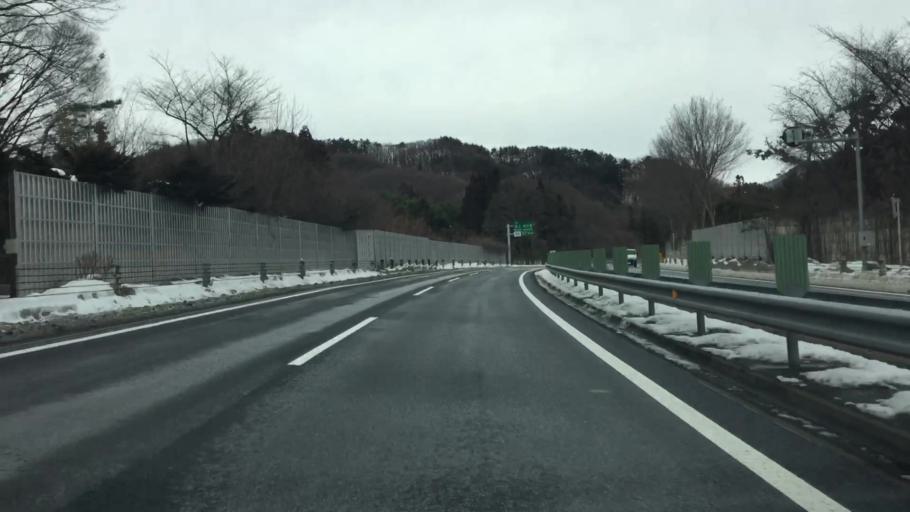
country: JP
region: Gunma
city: Numata
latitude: 36.7347
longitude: 138.9750
